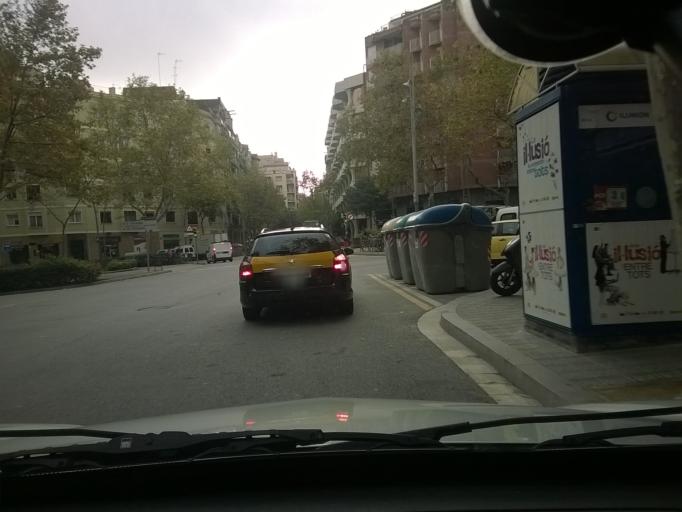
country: ES
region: Catalonia
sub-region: Provincia de Barcelona
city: Gracia
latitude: 41.4038
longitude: 2.1645
